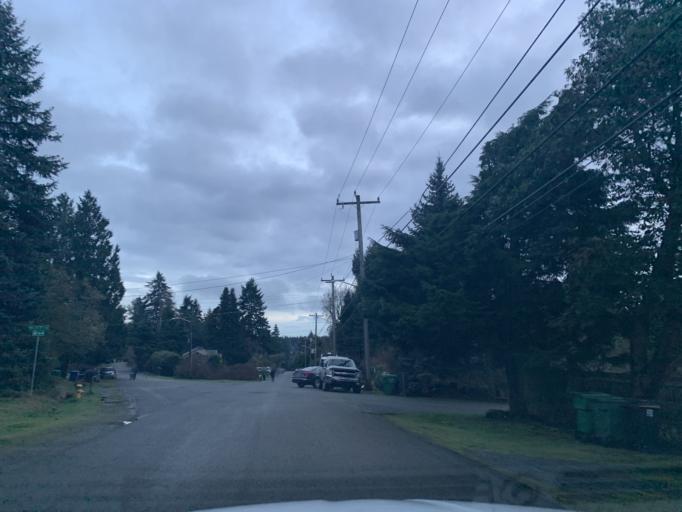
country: US
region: Washington
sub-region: King County
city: Lake Forest Park
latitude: 47.7140
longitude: -122.2853
